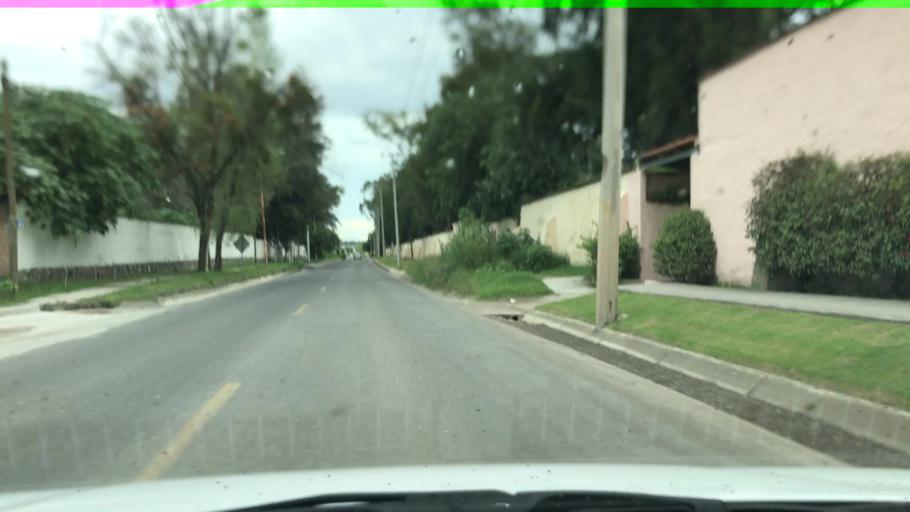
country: MX
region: Jalisco
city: Nicolas R Casillas
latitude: 20.5449
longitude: -103.4853
